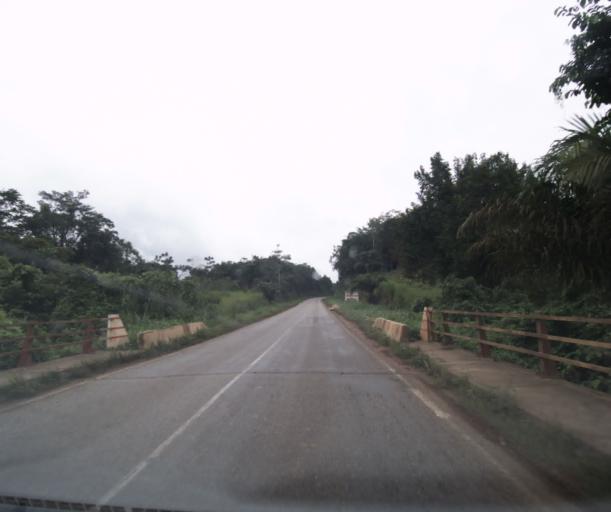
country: CM
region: Littoral
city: Edea
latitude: 3.8426
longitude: 10.4696
